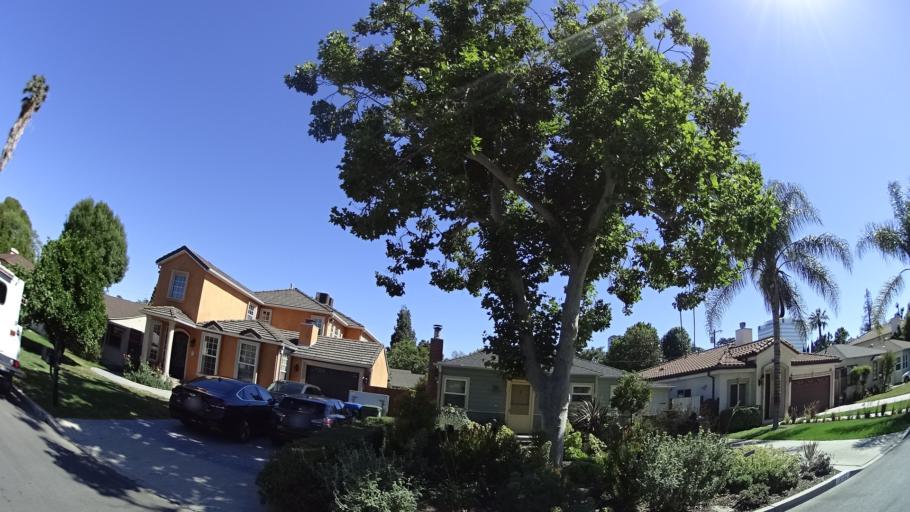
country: US
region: California
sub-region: Los Angeles County
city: Sherman Oaks
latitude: 34.1585
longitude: -118.4629
